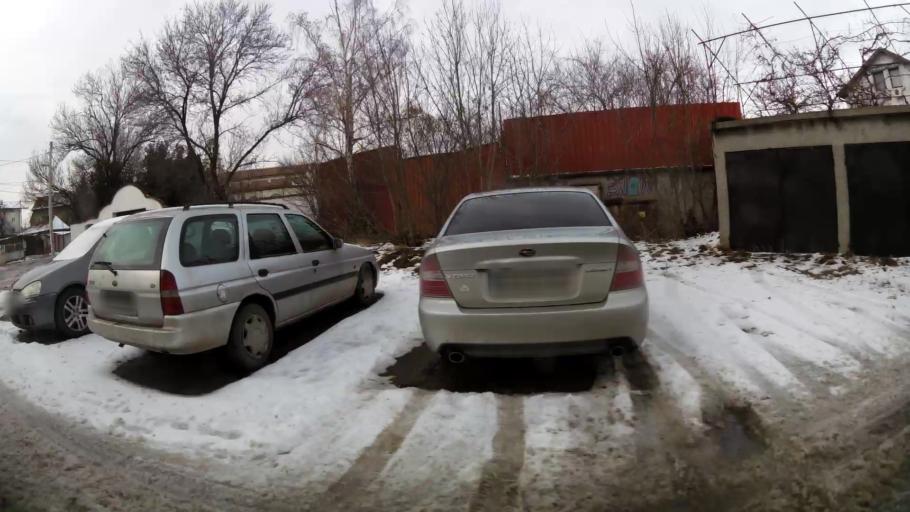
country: BG
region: Sofia-Capital
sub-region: Stolichna Obshtina
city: Sofia
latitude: 42.7171
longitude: 23.3480
